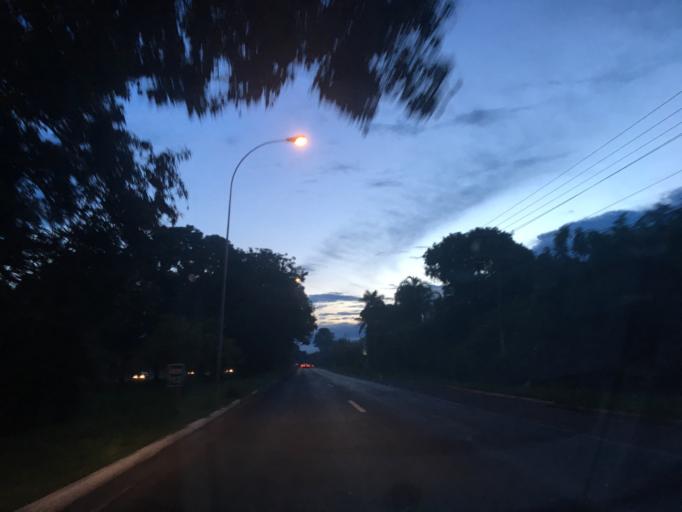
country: BR
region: Federal District
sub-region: Brasilia
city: Brasilia
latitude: -15.8445
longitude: -47.8720
